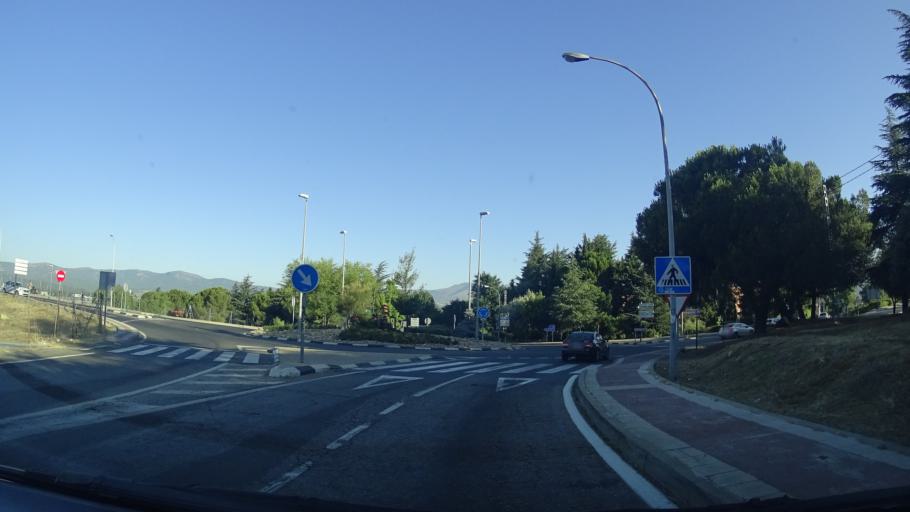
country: ES
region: Madrid
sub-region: Provincia de Madrid
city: Collado-Villalba
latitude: 40.6342
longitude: -4.0021
